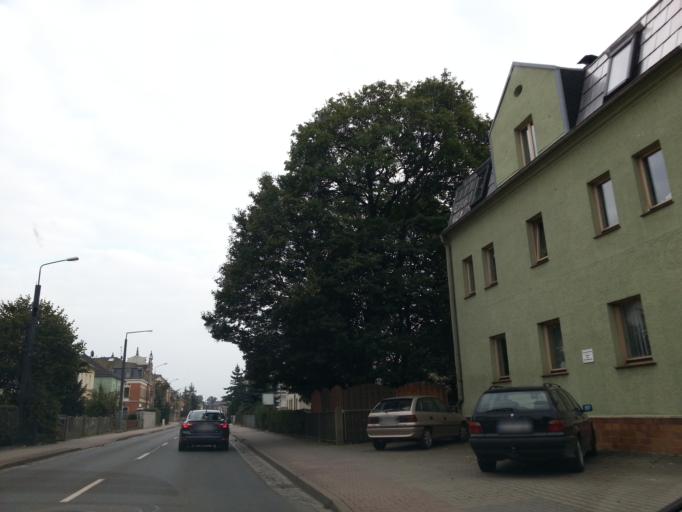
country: DE
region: Saxony
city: Radebeul
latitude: 51.0821
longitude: 13.6535
